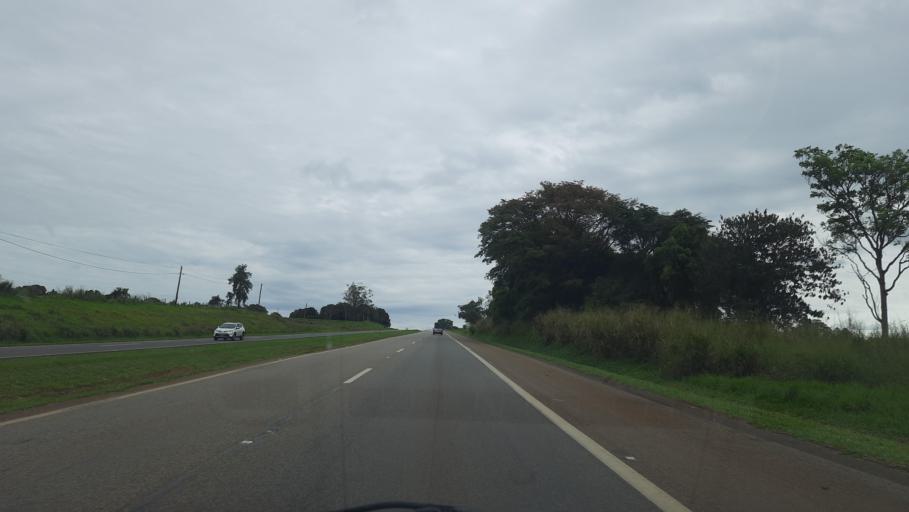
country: BR
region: Sao Paulo
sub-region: Moji-Guacu
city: Mogi-Gaucu
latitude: -22.2484
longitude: -46.9779
